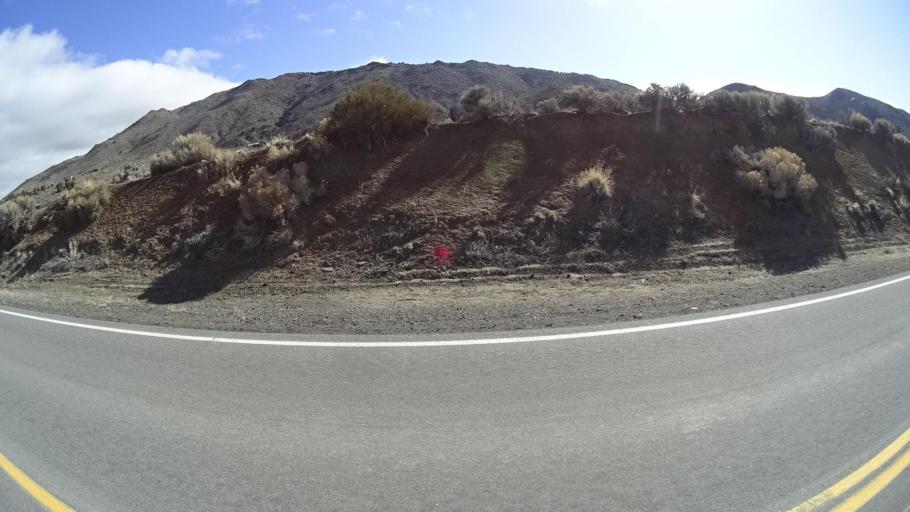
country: US
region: Nevada
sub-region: Washoe County
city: Cold Springs
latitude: 39.7595
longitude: -119.8859
